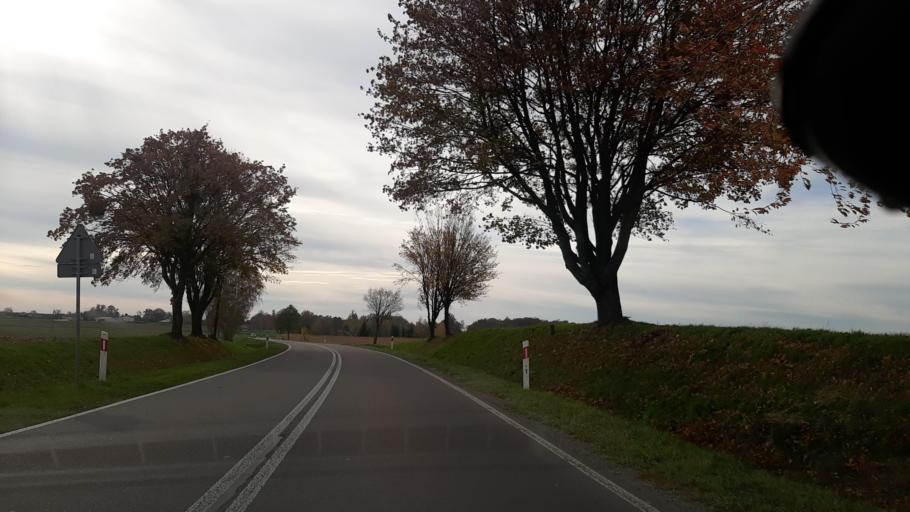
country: PL
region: Lublin Voivodeship
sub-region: Powiat pulawski
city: Markuszow
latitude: 51.3375
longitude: 22.2553
